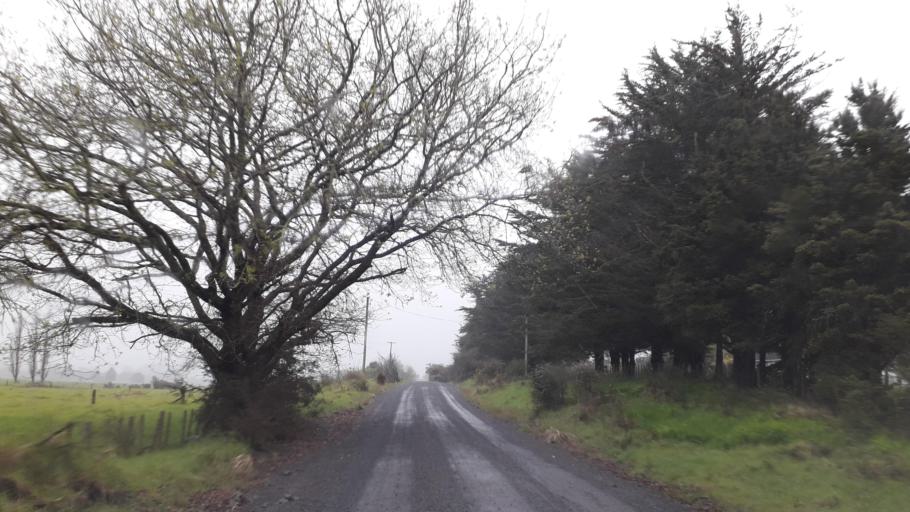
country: NZ
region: Northland
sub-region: Far North District
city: Waimate North
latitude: -35.4922
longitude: 173.6999
